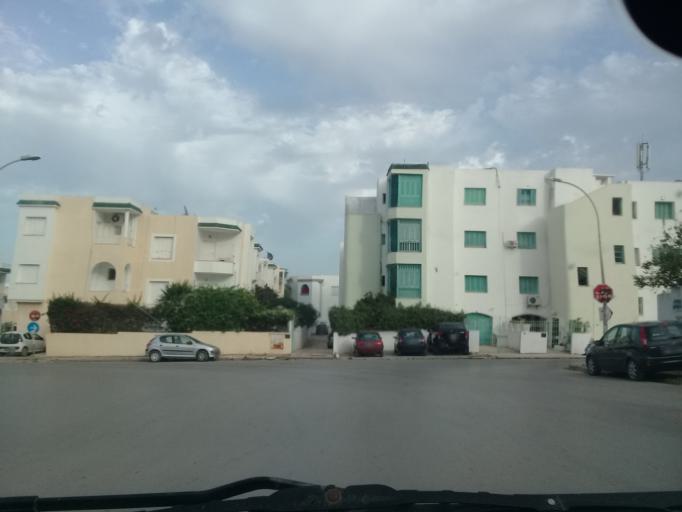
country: TN
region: Ariana
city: Ariana
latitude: 36.8635
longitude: 10.1685
